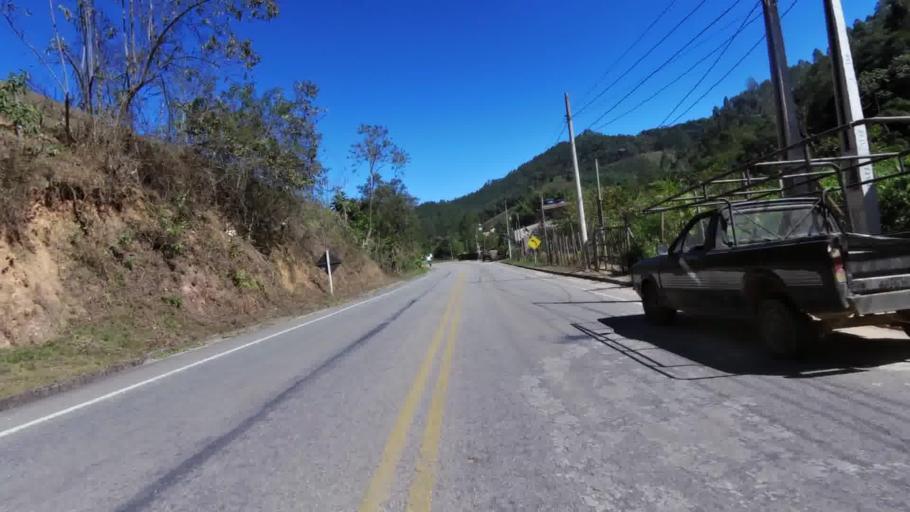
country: BR
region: Espirito Santo
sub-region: Vargem Alta
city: Vargem Alta
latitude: -20.6604
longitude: -40.9726
